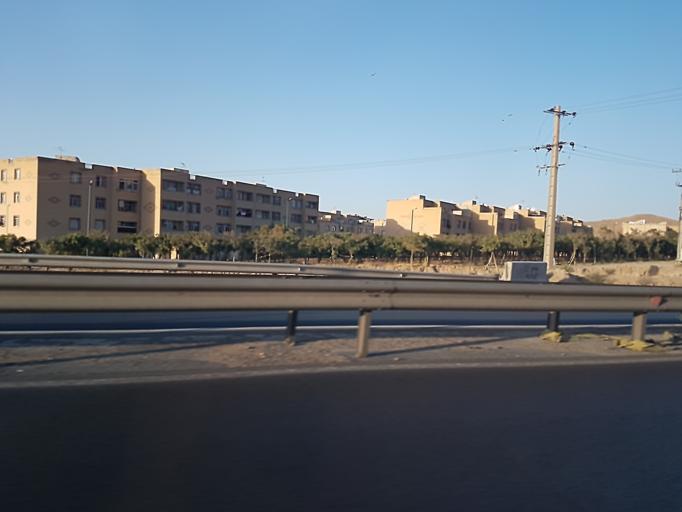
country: IR
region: Markazi
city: Arak
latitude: 34.0680
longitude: 49.7172
